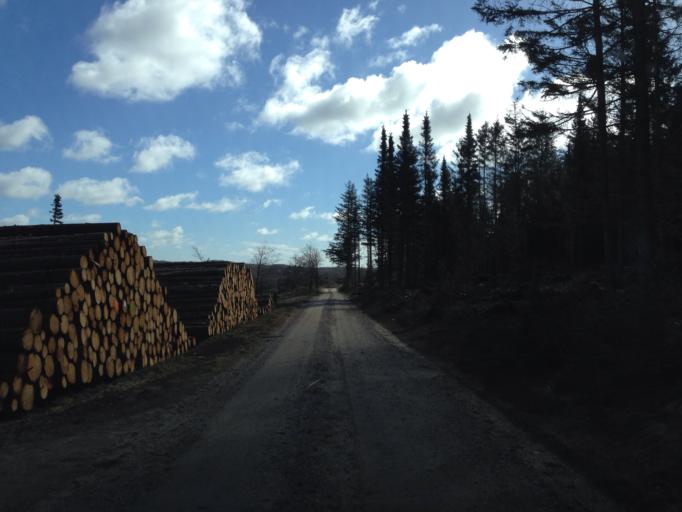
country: DK
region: Central Jutland
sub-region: Holstebro Kommune
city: Holstebro
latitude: 56.2555
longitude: 8.4988
